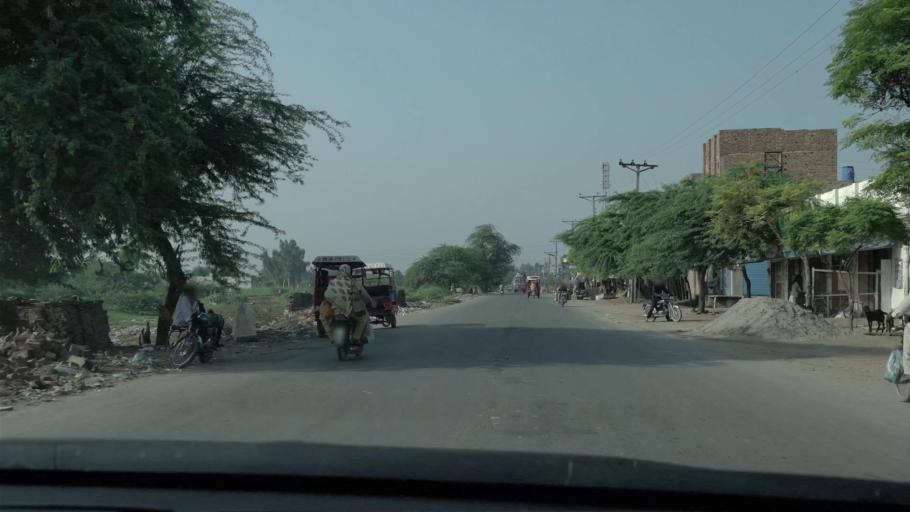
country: PK
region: Punjab
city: Gojra
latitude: 31.1226
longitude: 72.6704
